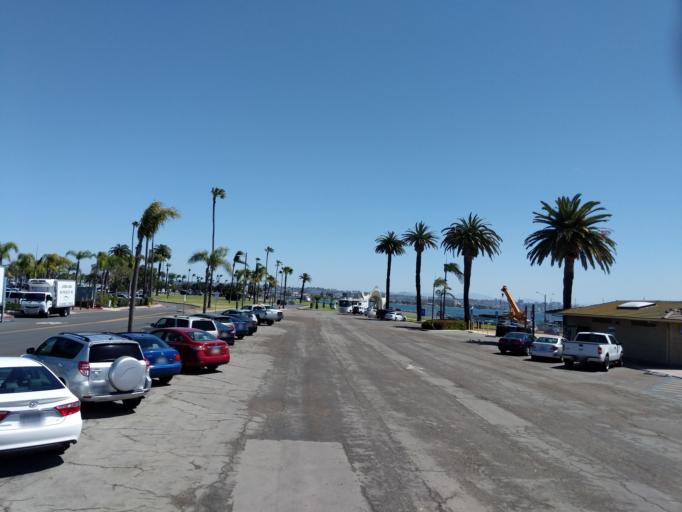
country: US
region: California
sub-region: San Diego County
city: Coronado
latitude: 32.7160
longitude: -117.2238
